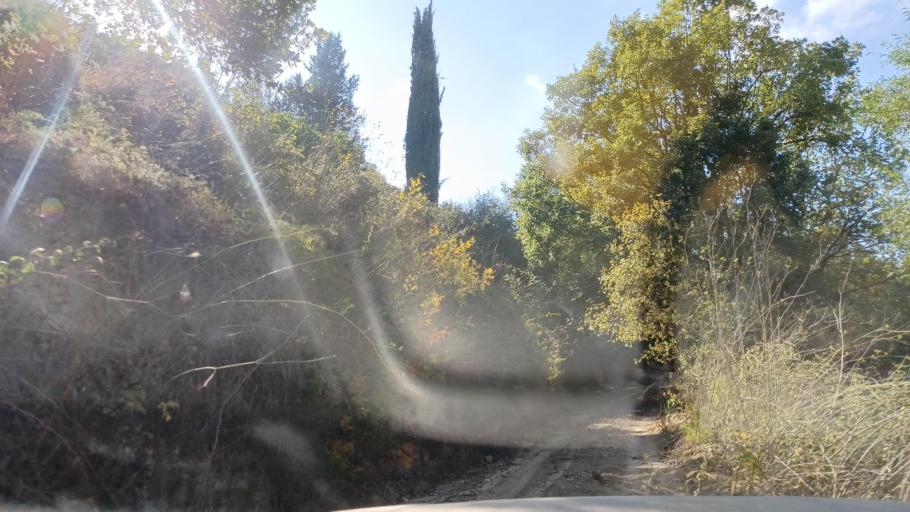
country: CY
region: Pafos
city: Pegeia
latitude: 34.9199
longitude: 32.4601
